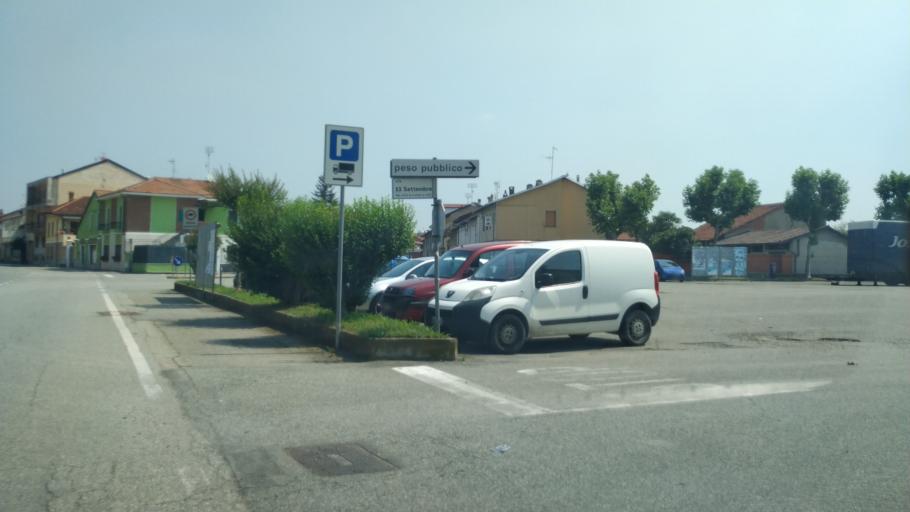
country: IT
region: Piedmont
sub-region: Provincia di Torino
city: Rondissone
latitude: 45.2446
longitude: 7.9630
